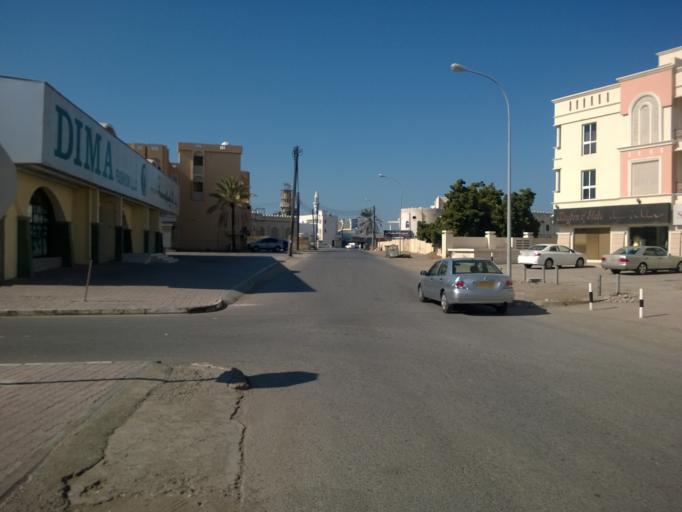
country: OM
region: Muhafazat Masqat
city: As Sib al Jadidah
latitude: 23.6827
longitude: 58.1867
